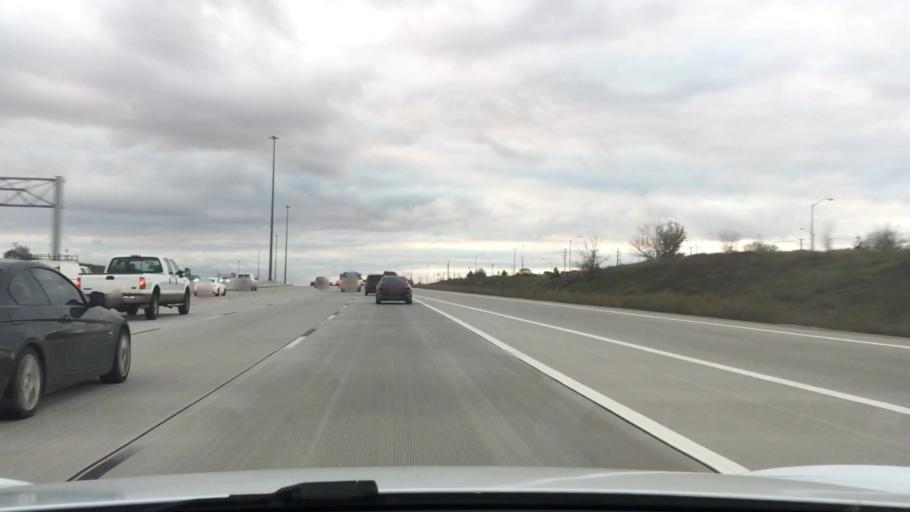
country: CA
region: Ontario
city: Concord
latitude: 43.8267
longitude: -79.4597
